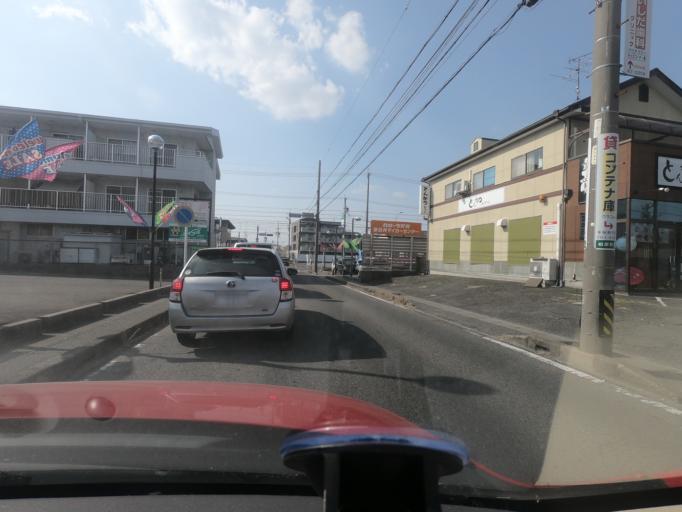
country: JP
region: Aichi
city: Kasugai
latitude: 35.2499
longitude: 136.9676
